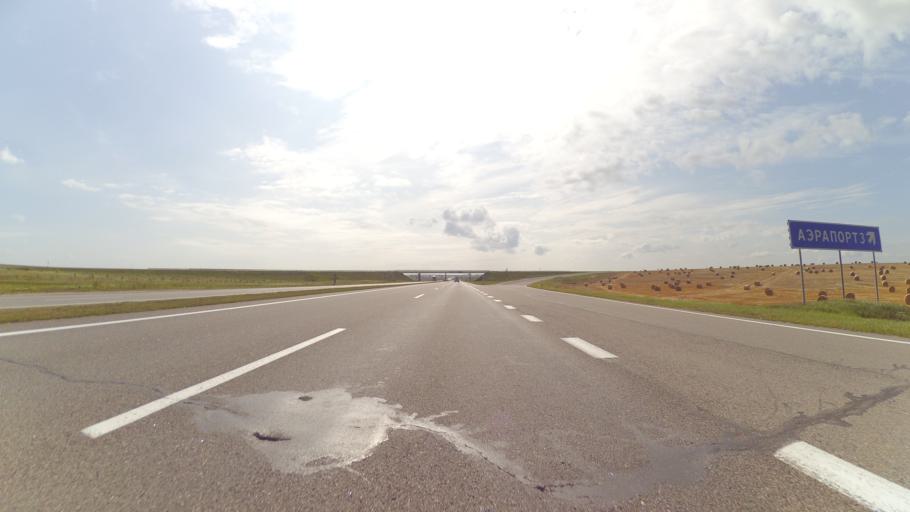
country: BY
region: Grodnenskaya
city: Skidal'
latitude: 53.6291
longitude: 24.0401
